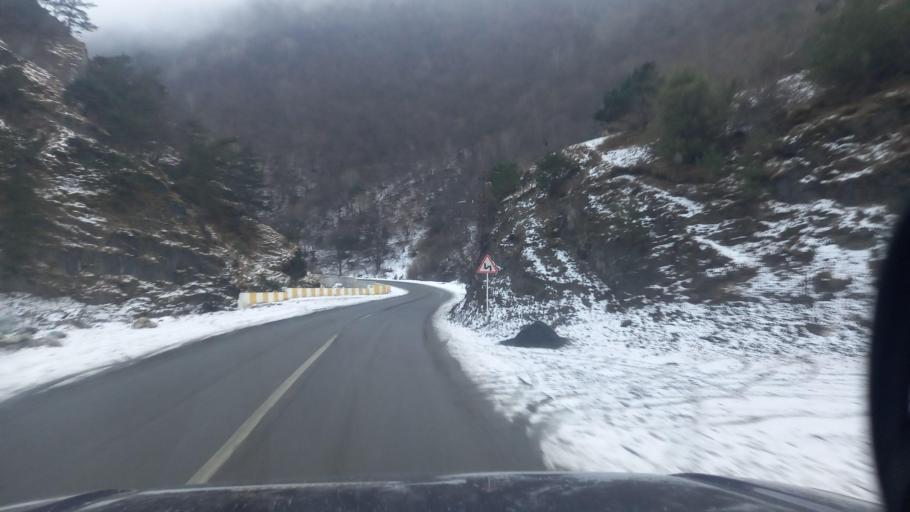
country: RU
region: Ingushetiya
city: Dzhayrakh
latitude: 42.7946
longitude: 44.7629
